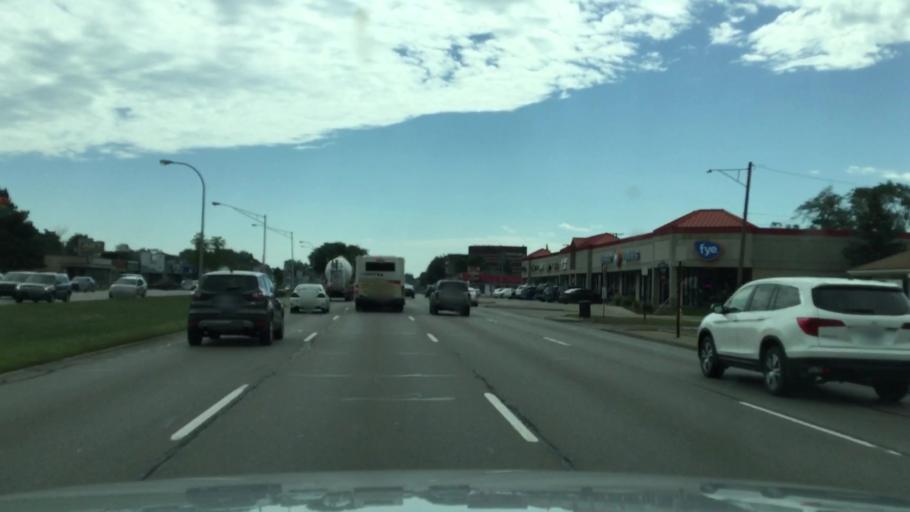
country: US
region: Michigan
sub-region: Oakland County
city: Berkley
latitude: 42.4988
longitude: -83.1679
